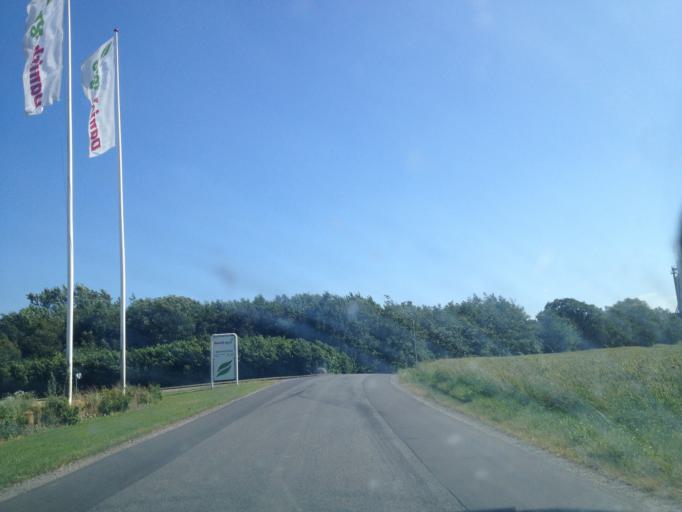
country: DK
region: South Denmark
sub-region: Kolding Kommune
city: Christiansfeld
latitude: 55.4024
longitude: 9.5253
